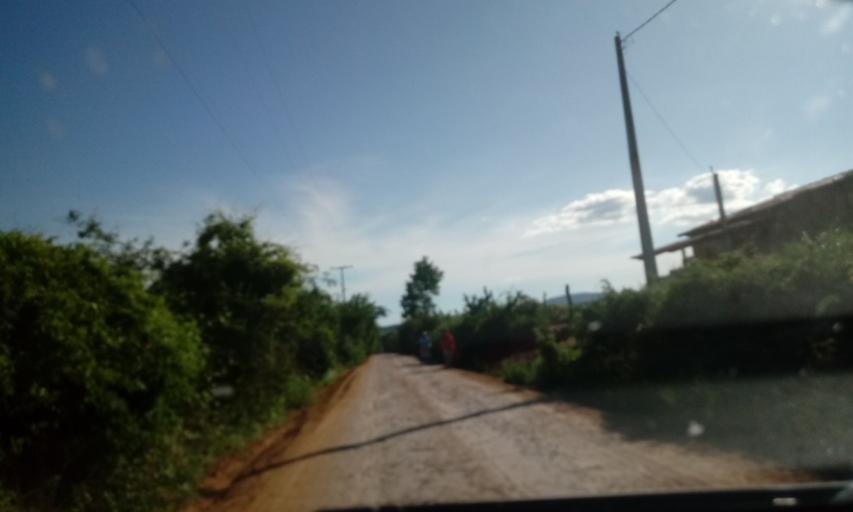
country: BR
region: Bahia
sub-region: Riacho De Santana
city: Riacho de Santana
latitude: -13.7852
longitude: -42.7254
